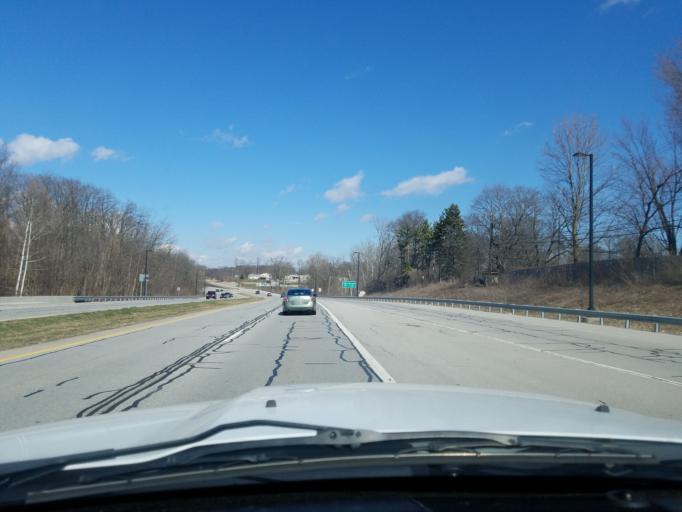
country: US
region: Indiana
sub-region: Hamilton County
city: Carmel
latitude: 39.9805
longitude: -86.1127
